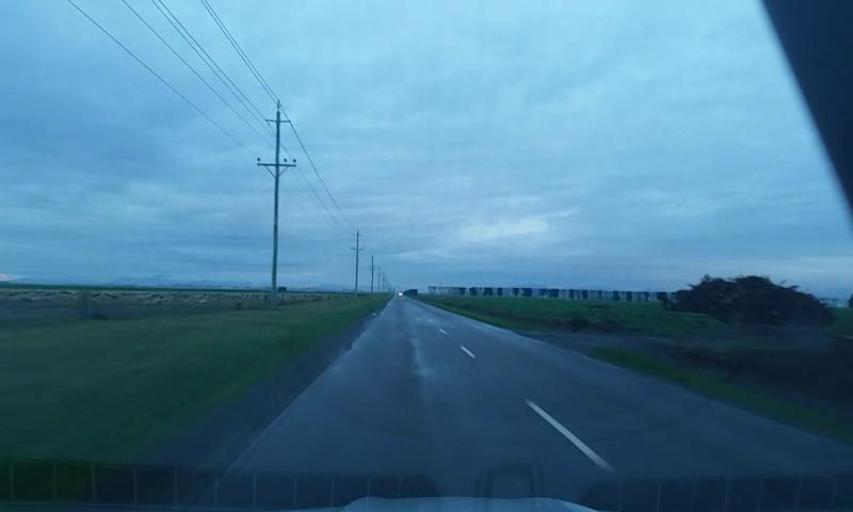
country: NZ
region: Canterbury
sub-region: Ashburton District
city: Rakaia
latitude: -43.7566
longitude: 171.9340
